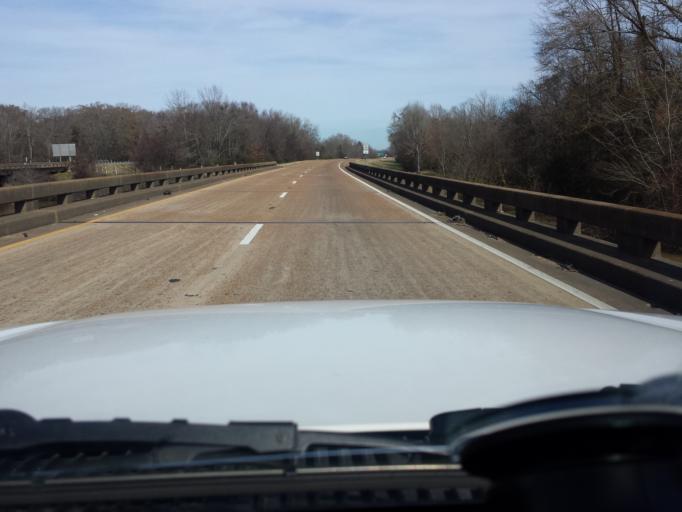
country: US
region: Mississippi
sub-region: Madison County
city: Canton
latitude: 32.6145
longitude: -90.0678
